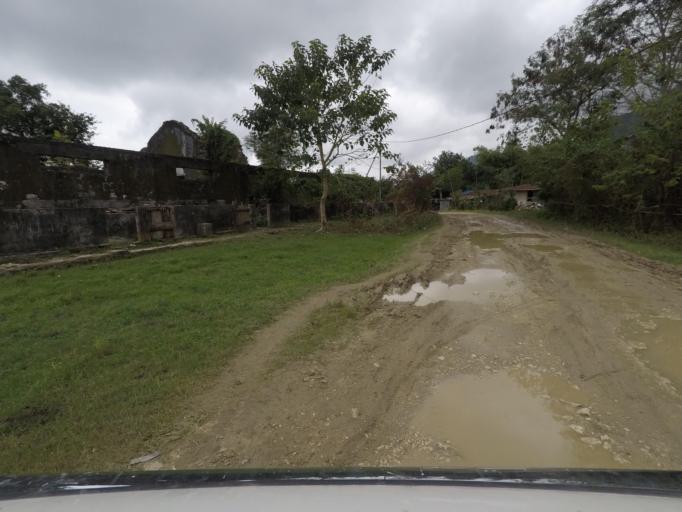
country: TL
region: Baucau
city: Venilale
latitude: -8.7359
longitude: 126.3690
